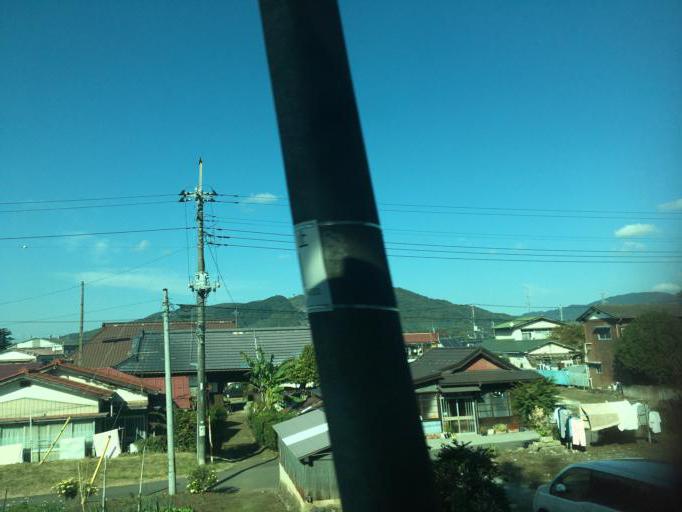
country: JP
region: Ibaraki
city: Iwase
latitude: 36.3600
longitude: 140.1041
